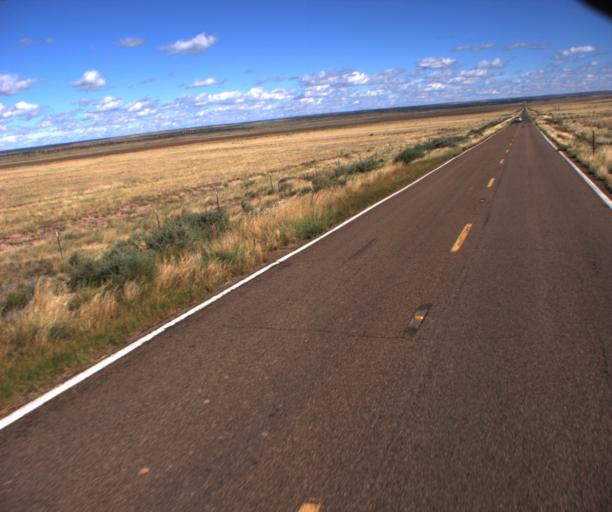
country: US
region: Arizona
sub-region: Apache County
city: Saint Johns
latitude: 34.6677
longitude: -109.2897
